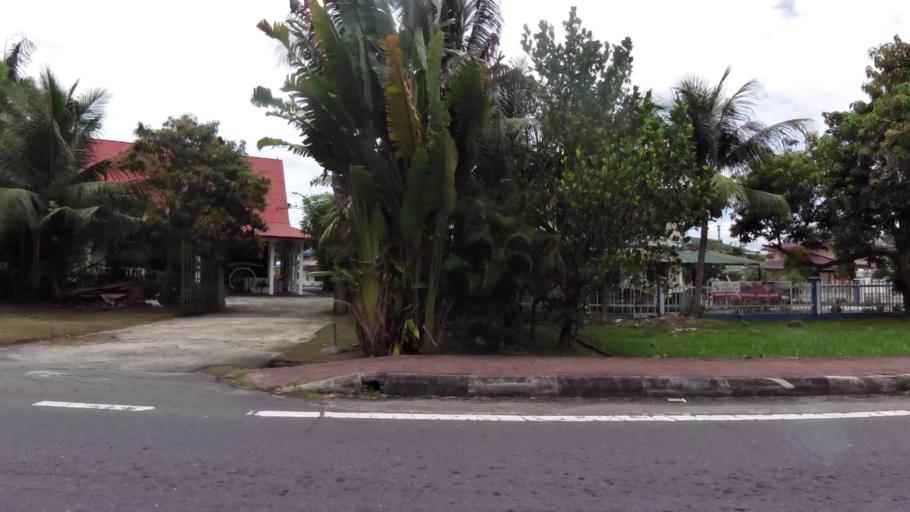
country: BN
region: Brunei and Muara
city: Bandar Seri Begawan
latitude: 4.9133
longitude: 114.9132
